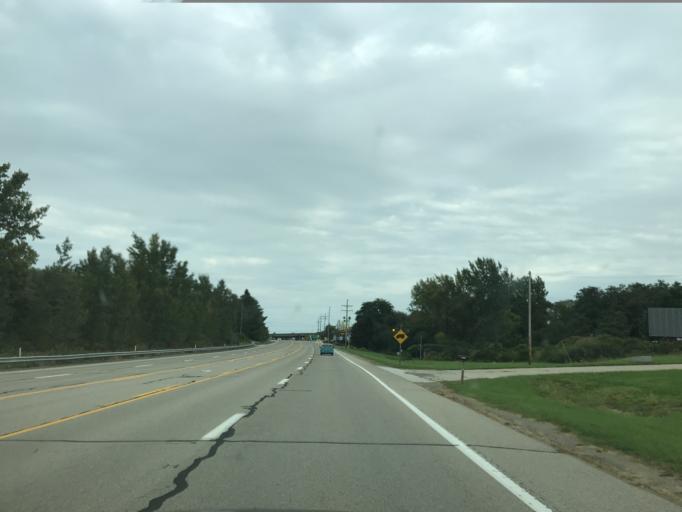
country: US
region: Pennsylvania
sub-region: Erie County
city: North East
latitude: 42.2310
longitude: -79.7865
